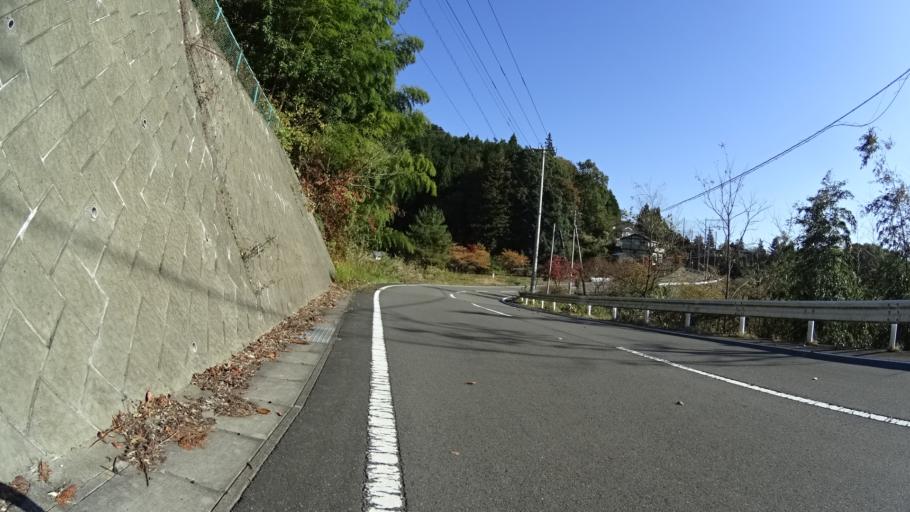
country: JP
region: Yamanashi
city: Uenohara
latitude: 35.6626
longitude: 139.1164
